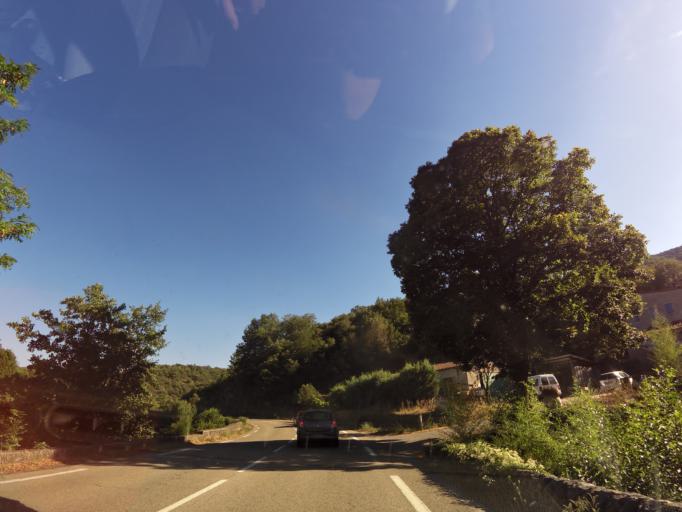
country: FR
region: Languedoc-Roussillon
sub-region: Departement du Gard
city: Valleraugue
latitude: 44.0393
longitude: 3.6720
